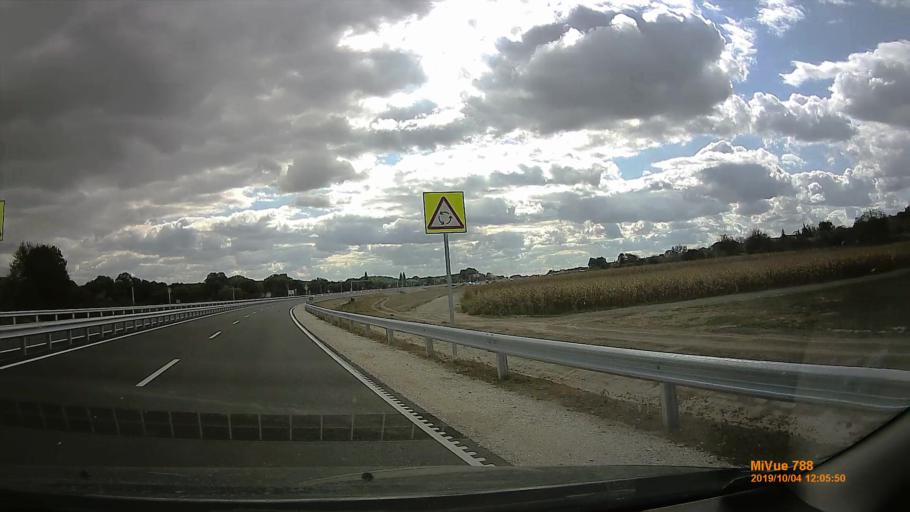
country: HU
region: Somogy
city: Karad
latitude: 46.5570
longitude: 17.8123
